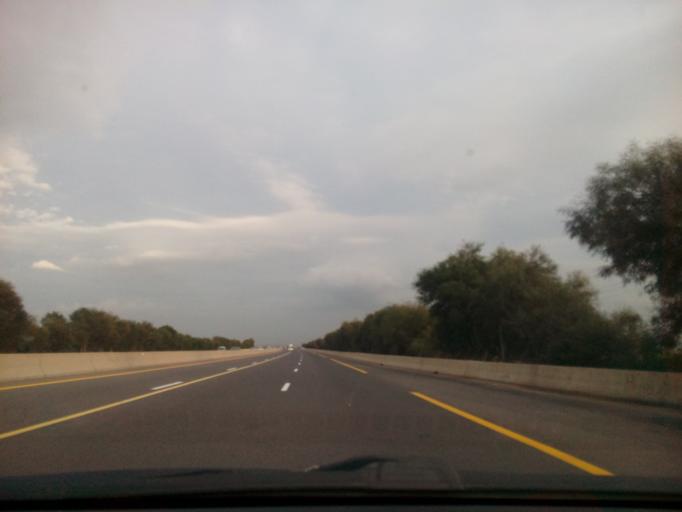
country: DZ
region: Relizane
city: Relizane
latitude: 35.7907
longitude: 0.4624
